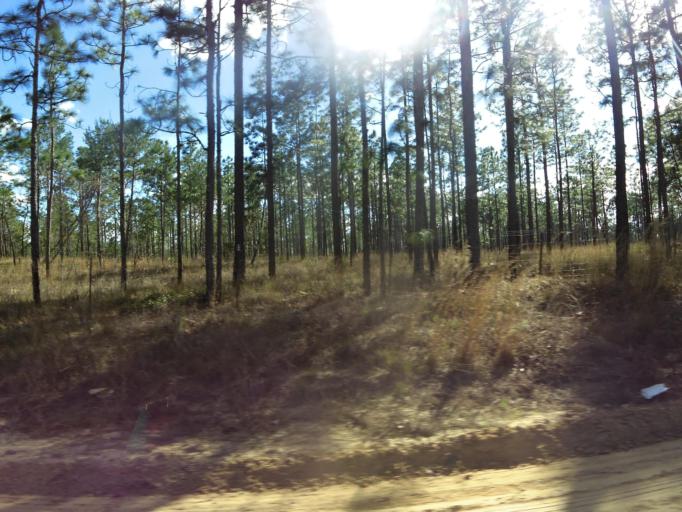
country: US
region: Florida
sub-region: Putnam County
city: Interlachen
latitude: 29.7854
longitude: -81.8684
